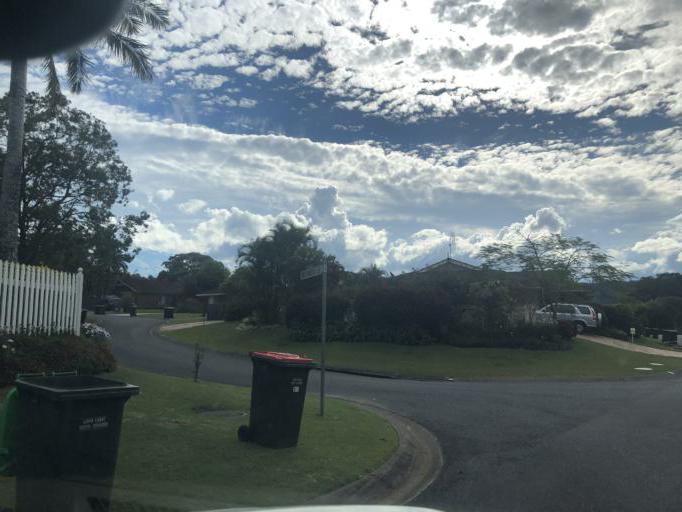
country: AU
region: New South Wales
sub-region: Coffs Harbour
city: Coffs Harbour
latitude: -30.2906
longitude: 153.0986
